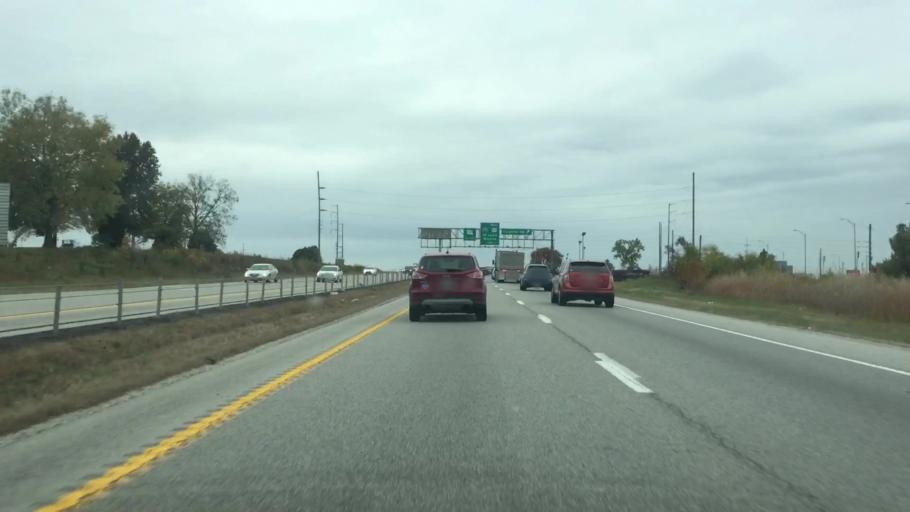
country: US
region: Missouri
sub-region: Jackson County
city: Lees Summit
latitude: 38.9210
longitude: -94.4022
